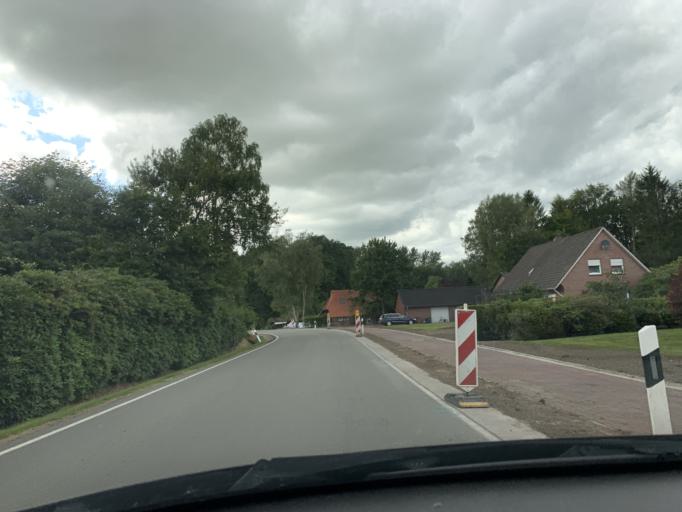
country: DE
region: Lower Saxony
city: Westerstede
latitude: 53.2122
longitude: 7.9306
